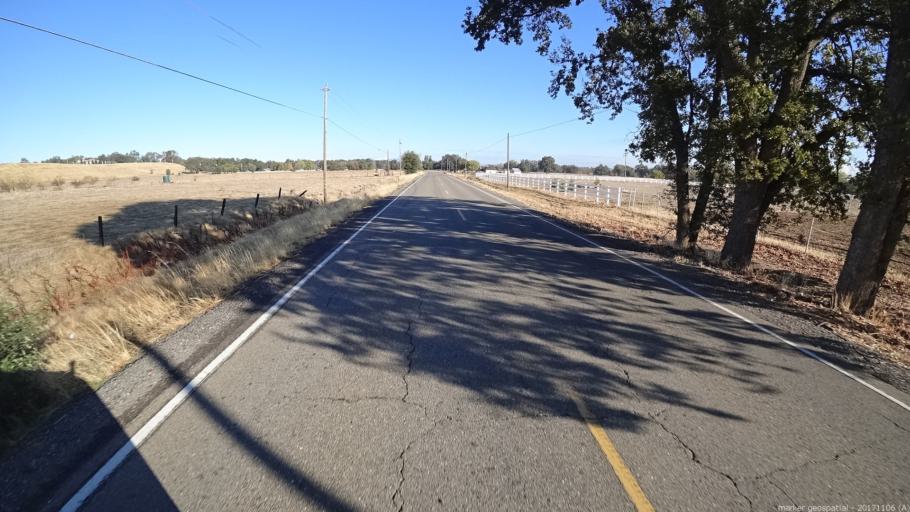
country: US
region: California
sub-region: Shasta County
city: Anderson
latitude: 40.4871
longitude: -122.2392
